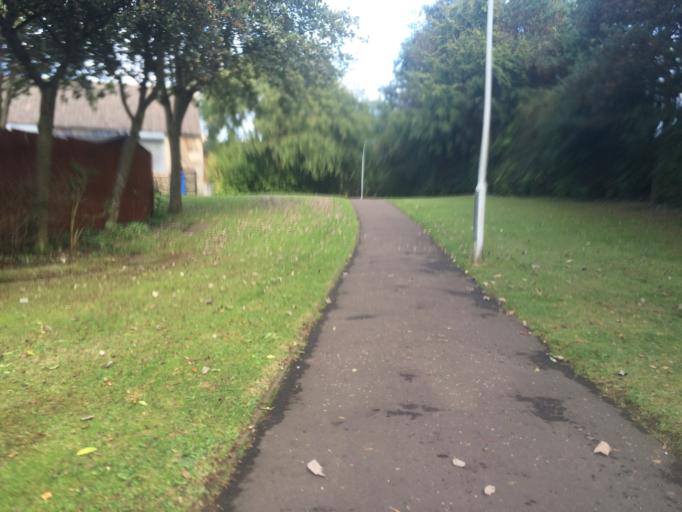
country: GB
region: Scotland
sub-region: Fife
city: Glenrothes
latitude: 56.2123
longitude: -3.1874
